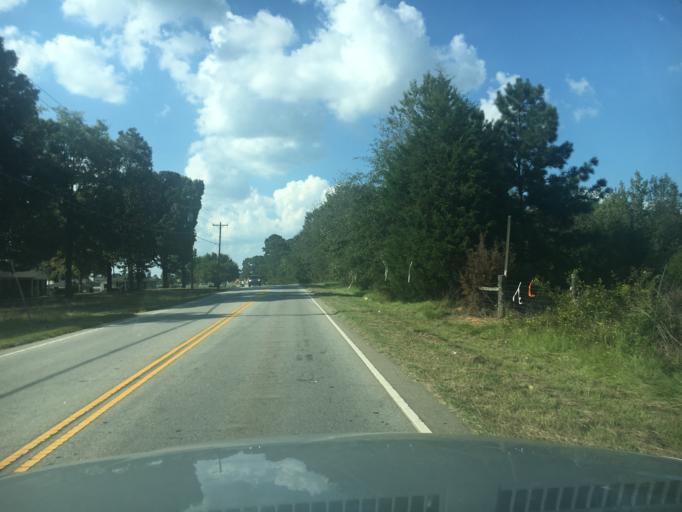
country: US
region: South Carolina
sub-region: Greenville County
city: Simpsonville
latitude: 34.6974
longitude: -82.2546
